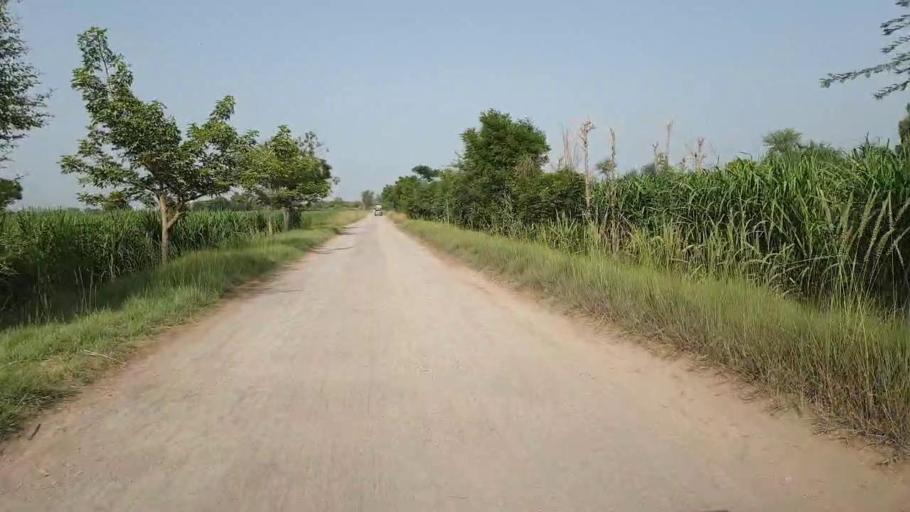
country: PK
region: Sindh
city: Daur
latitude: 26.3223
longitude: 68.1487
